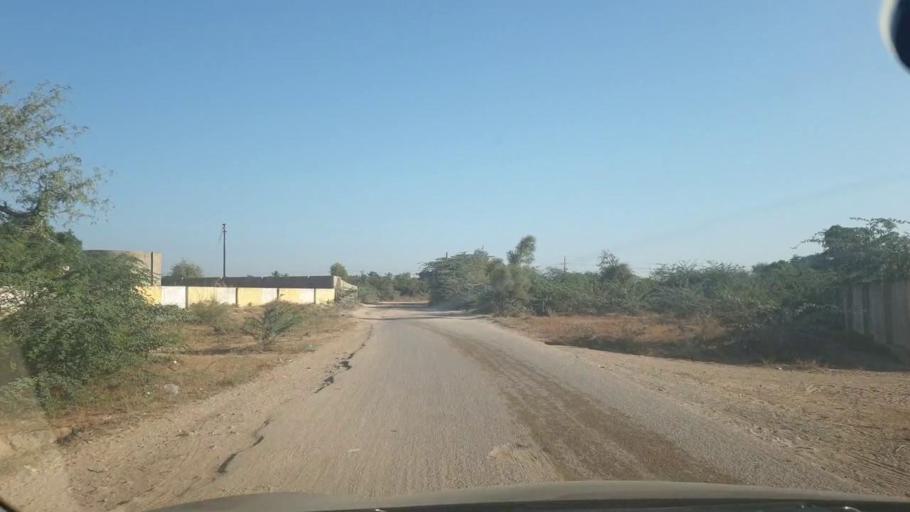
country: PK
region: Sindh
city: Malir Cantonment
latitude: 25.1025
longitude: 67.2571
